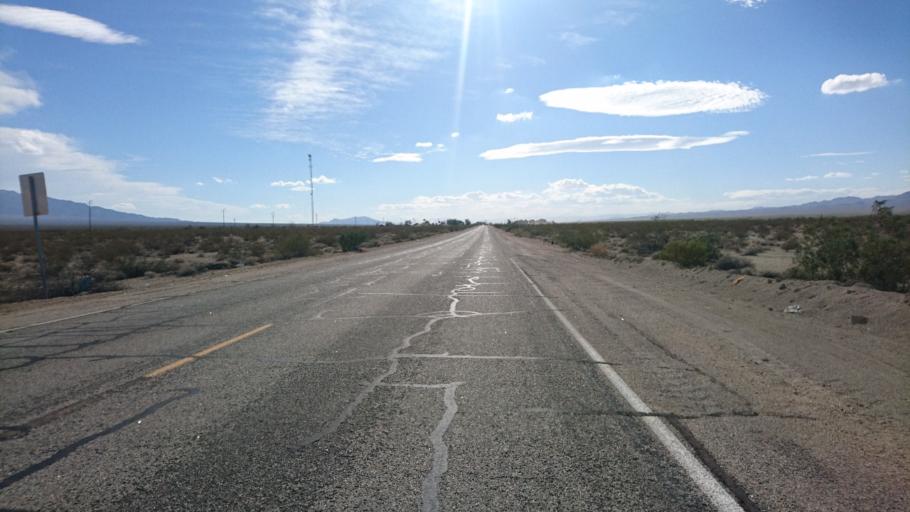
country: US
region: California
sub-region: San Bernardino County
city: Needles
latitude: 34.7402
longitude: -115.2405
